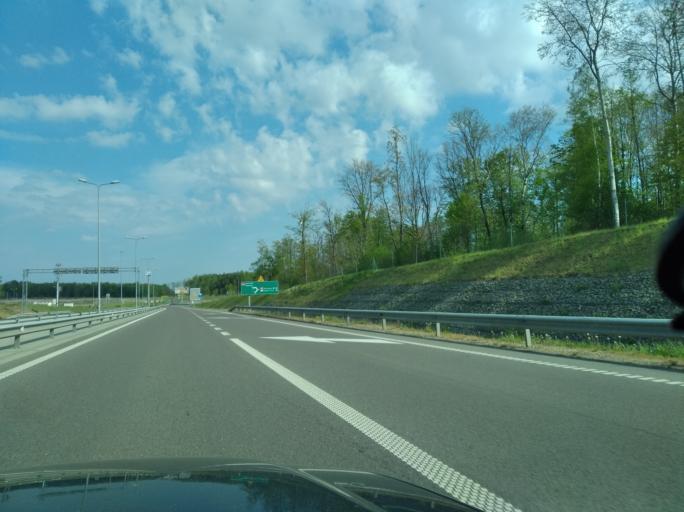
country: PL
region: Subcarpathian Voivodeship
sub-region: Powiat lubaczowski
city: Wielkie Oczy
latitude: 49.9649
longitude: 23.0687
